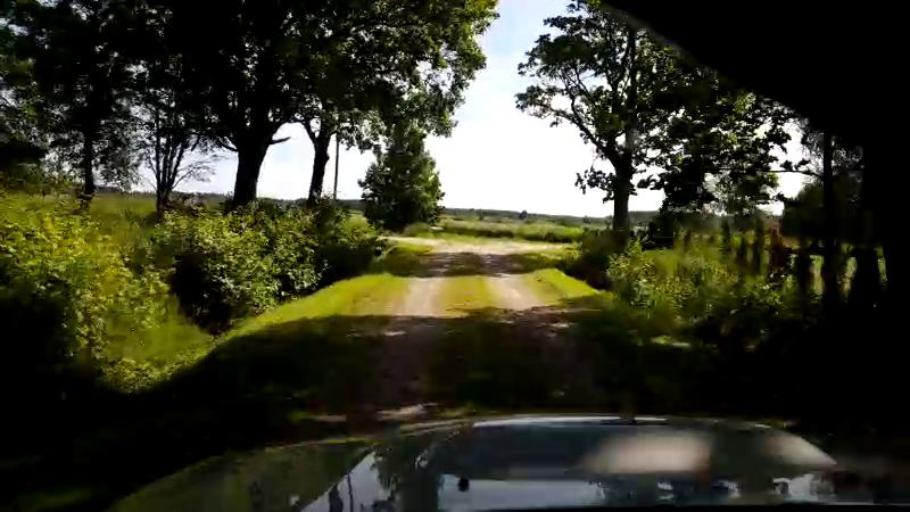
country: EE
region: Paernumaa
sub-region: Sauga vald
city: Sauga
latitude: 58.4757
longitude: 24.5355
